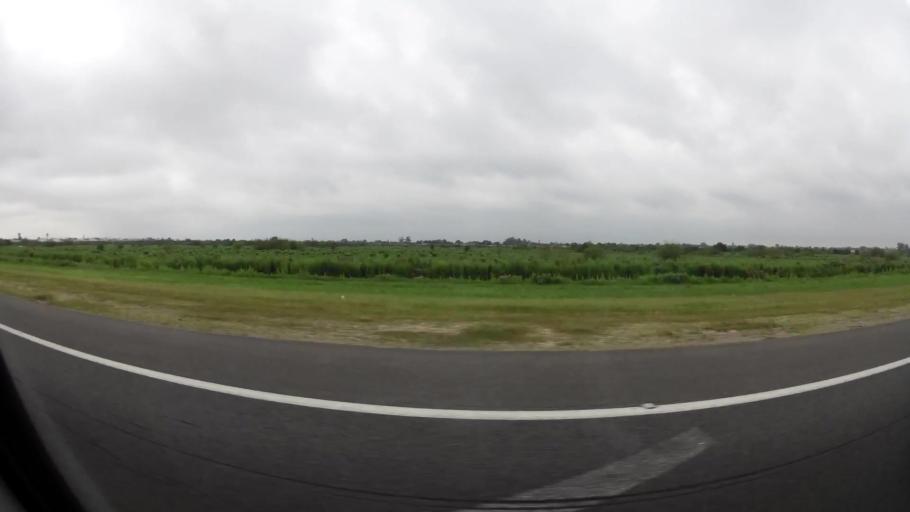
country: AR
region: Buenos Aires
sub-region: Partido de La Plata
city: La Plata
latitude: -34.8712
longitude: -57.9851
